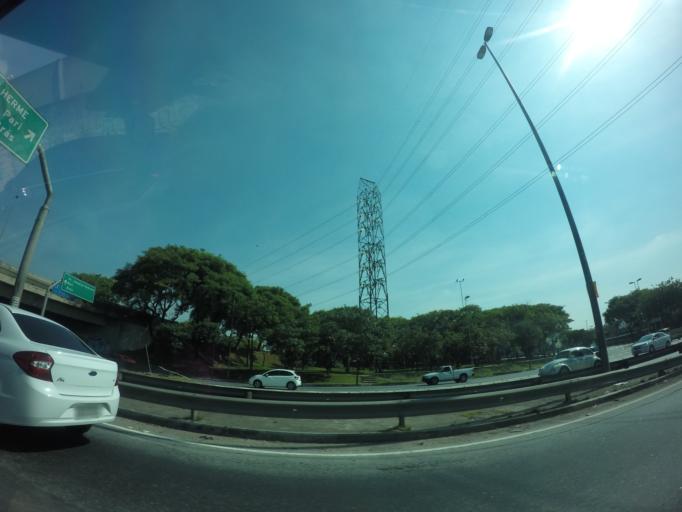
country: BR
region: Sao Paulo
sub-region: Sao Paulo
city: Sao Paulo
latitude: -23.5269
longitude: -46.5958
